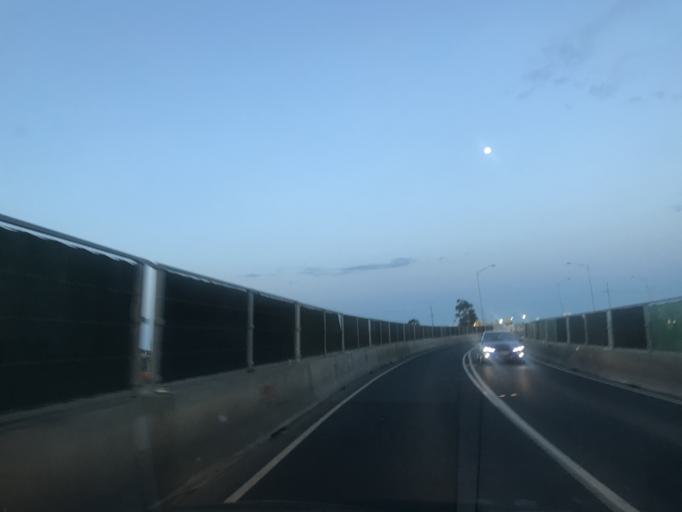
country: AU
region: Victoria
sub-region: Wyndham
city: Williams Landing
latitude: -37.8687
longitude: 144.7317
